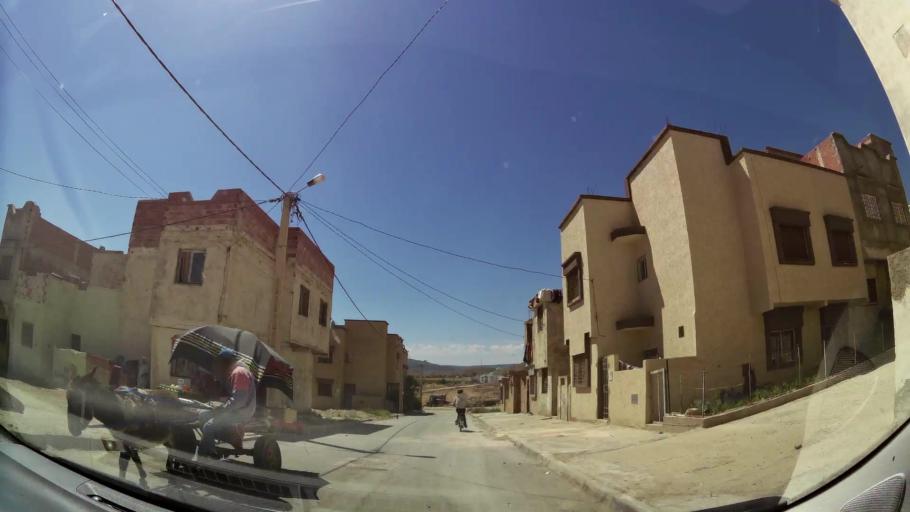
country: MA
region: Oriental
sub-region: Oujda-Angad
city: Oujda
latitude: 34.6515
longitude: -1.8678
